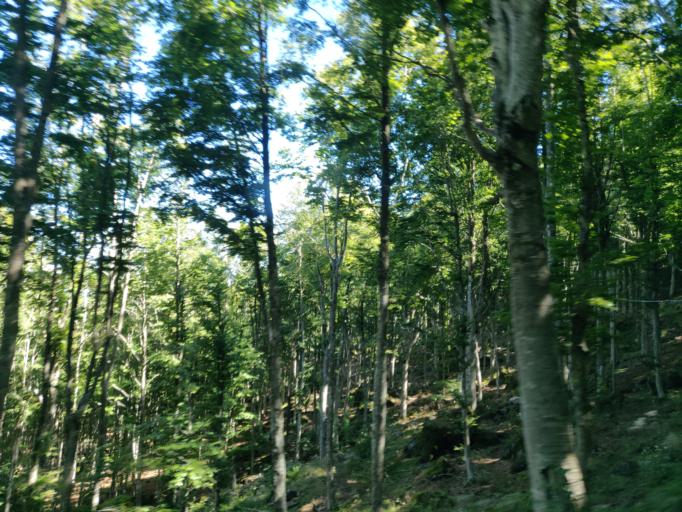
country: IT
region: Tuscany
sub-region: Provincia di Siena
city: Abbadia San Salvatore
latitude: 42.8960
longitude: 11.6289
